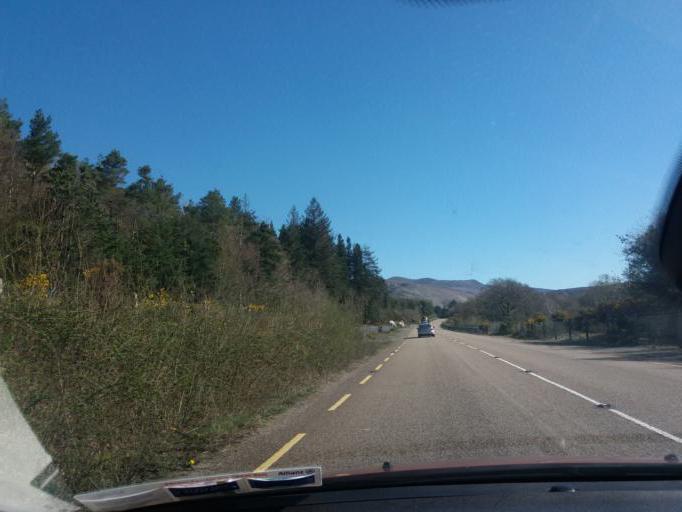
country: IE
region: Munster
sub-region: Ciarrai
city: Cill Airne
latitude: 51.9613
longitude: -9.3648
